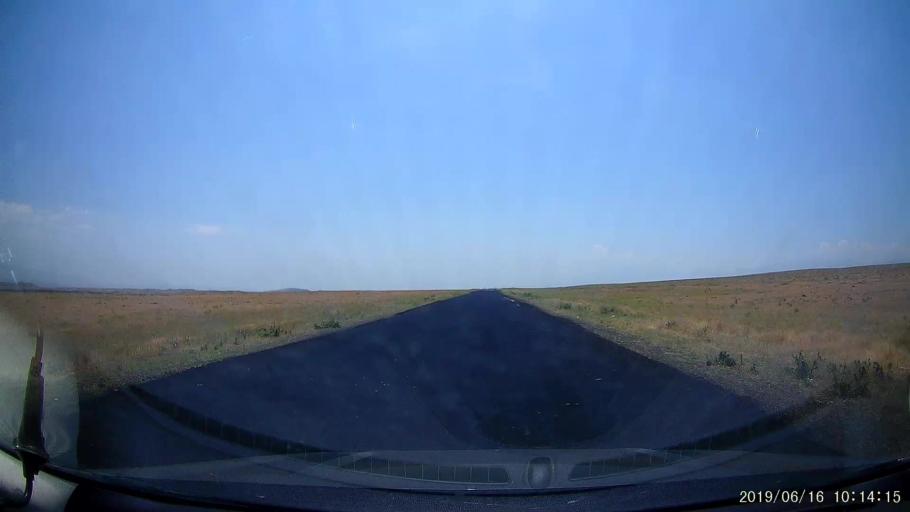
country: TR
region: Igdir
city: Tuzluca
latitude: 40.1864
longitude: 43.6589
